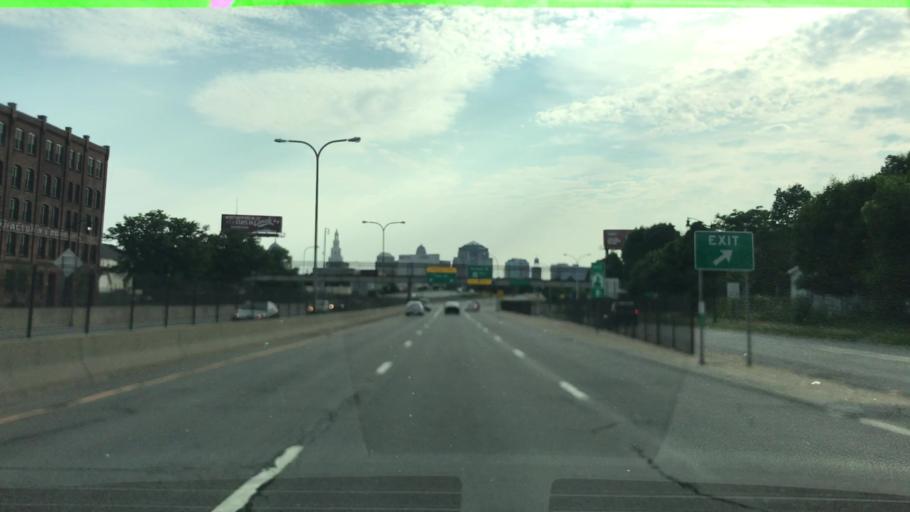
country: US
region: New York
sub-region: Erie County
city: Buffalo
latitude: 42.8948
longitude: -78.8606
